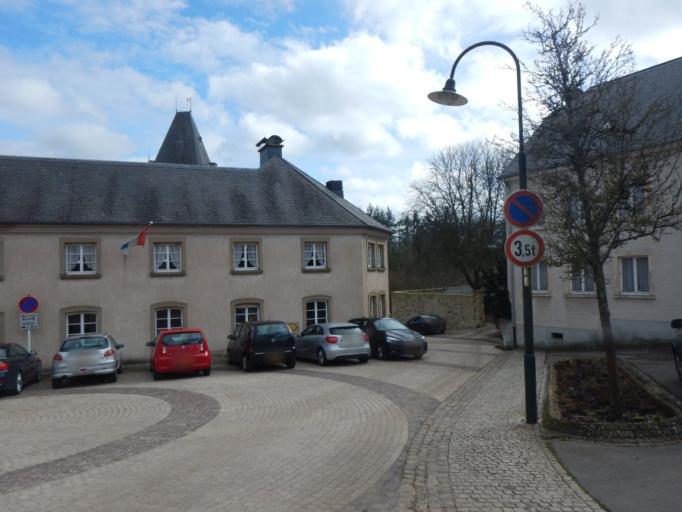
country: LU
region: Luxembourg
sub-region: Canton de Mersch
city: Tuntange
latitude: 49.7125
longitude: 6.0501
